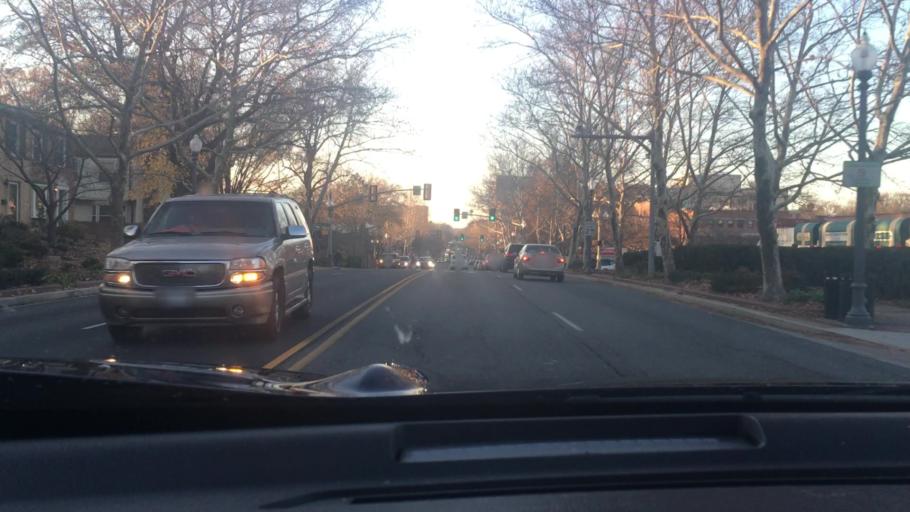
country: US
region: Virginia
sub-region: City of Falls Church
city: Falls Church
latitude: 38.8844
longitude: -77.1743
